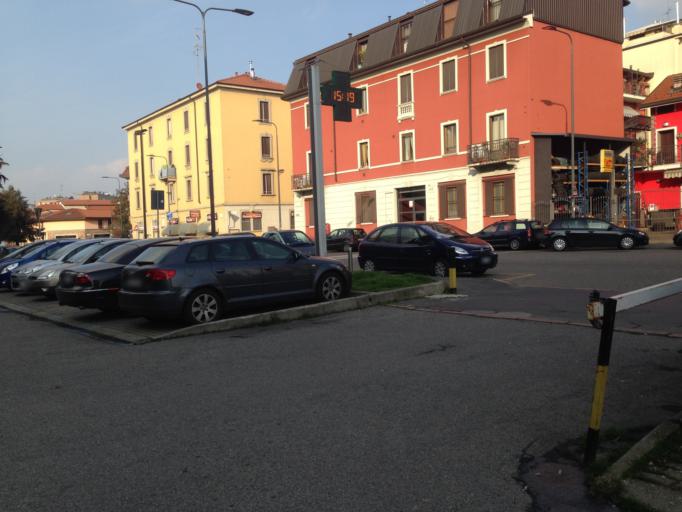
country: IT
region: Lombardy
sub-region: Citta metropolitana di Milano
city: Cesano Boscone
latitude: 45.4711
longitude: 9.1090
